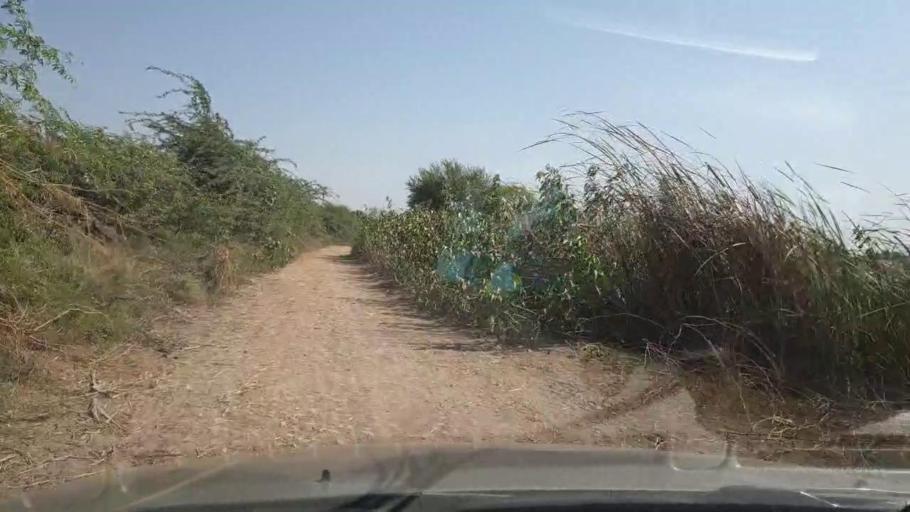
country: PK
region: Sindh
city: Daro Mehar
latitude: 24.9713
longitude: 68.1151
